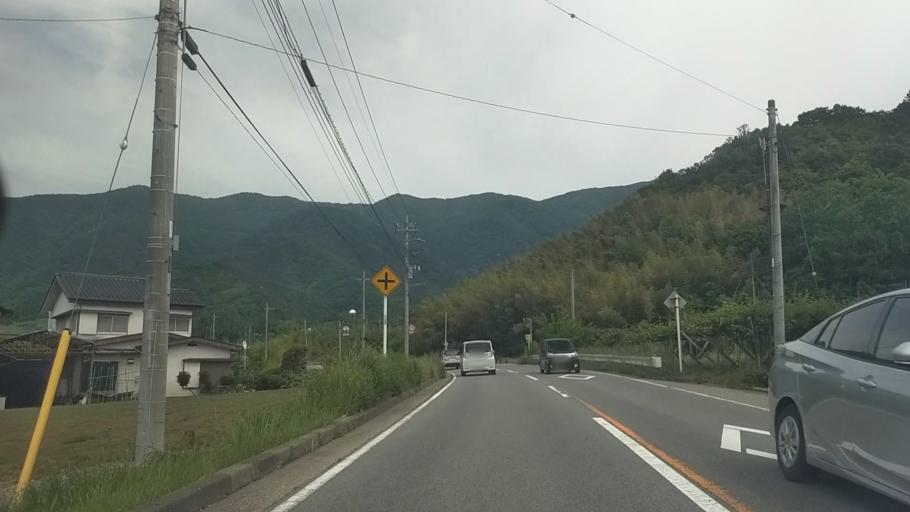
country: JP
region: Yamanashi
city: Isawa
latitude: 35.5708
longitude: 138.5934
